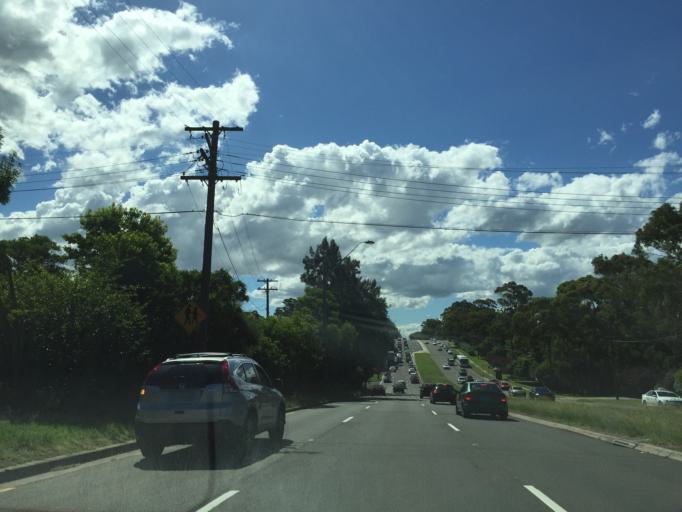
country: AU
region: New South Wales
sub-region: Ryde
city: Macquarie Park
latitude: -33.7805
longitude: 151.1118
